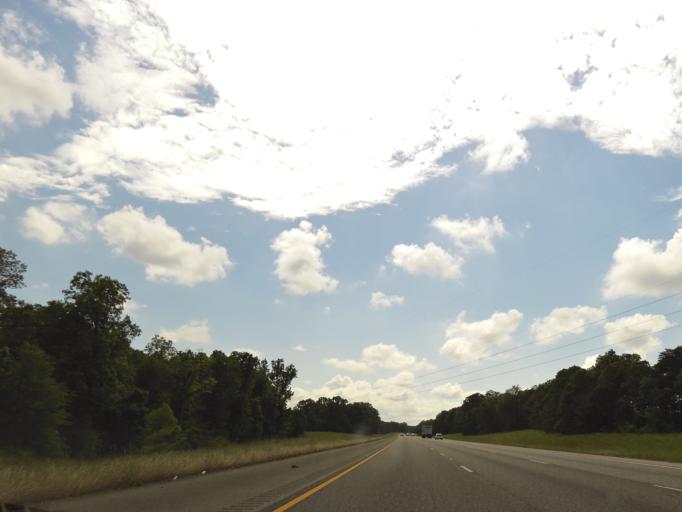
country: US
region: Alabama
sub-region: Calhoun County
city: Bynum
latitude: 33.5791
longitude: -85.9775
